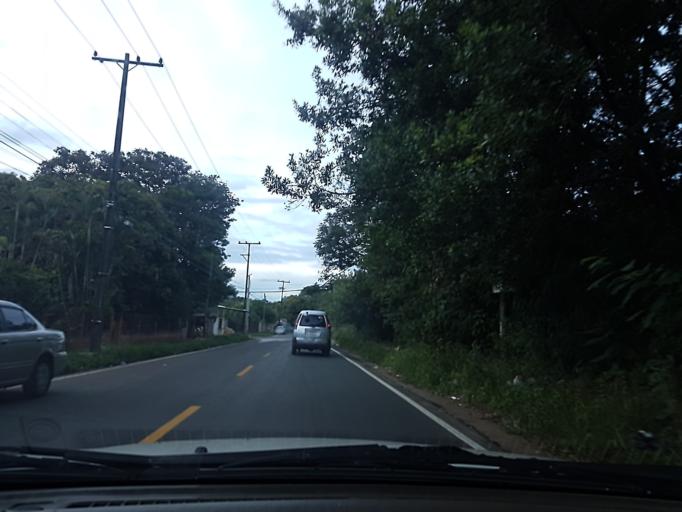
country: PY
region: Central
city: San Lorenzo
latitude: -25.2700
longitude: -57.4748
